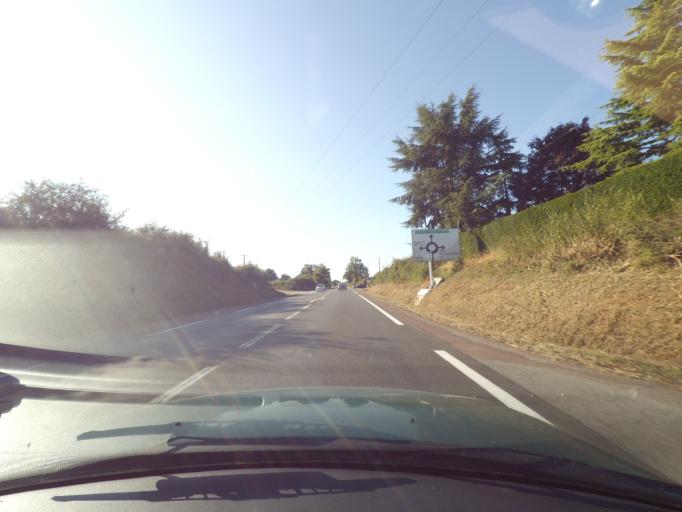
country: FR
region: Poitou-Charentes
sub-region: Departement des Deux-Sevres
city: Viennay
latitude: 46.6741
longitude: -0.2590
